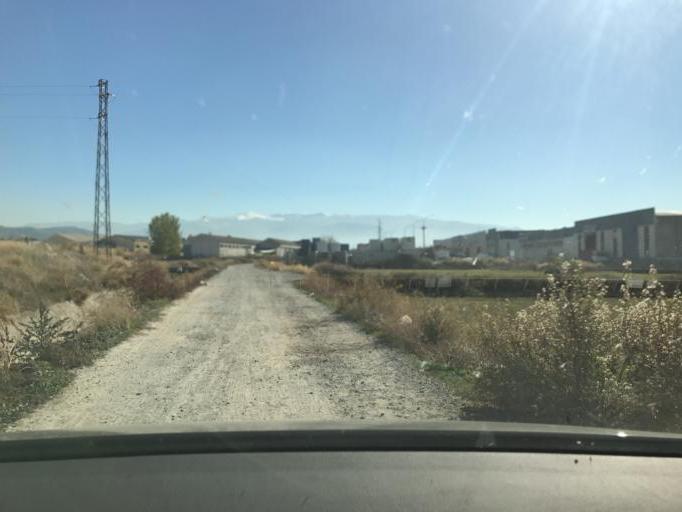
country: ES
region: Andalusia
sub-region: Provincia de Granada
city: Maracena
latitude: 37.2050
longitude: -3.6432
